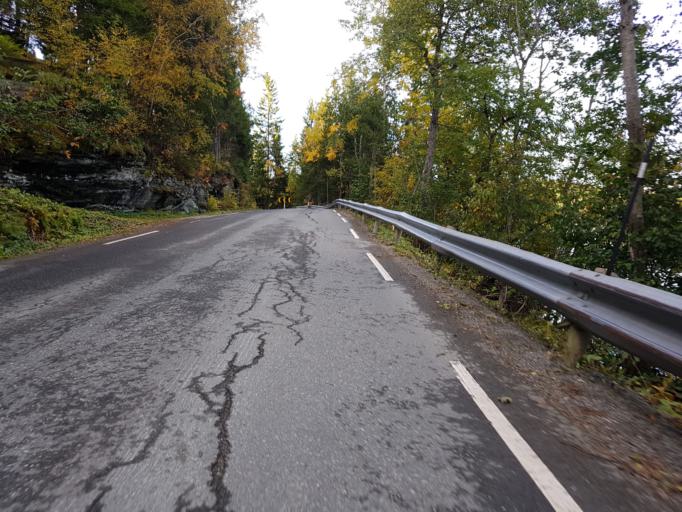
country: NO
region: Sor-Trondelag
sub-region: Klaebu
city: Klaebu
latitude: 63.3417
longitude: 10.5579
